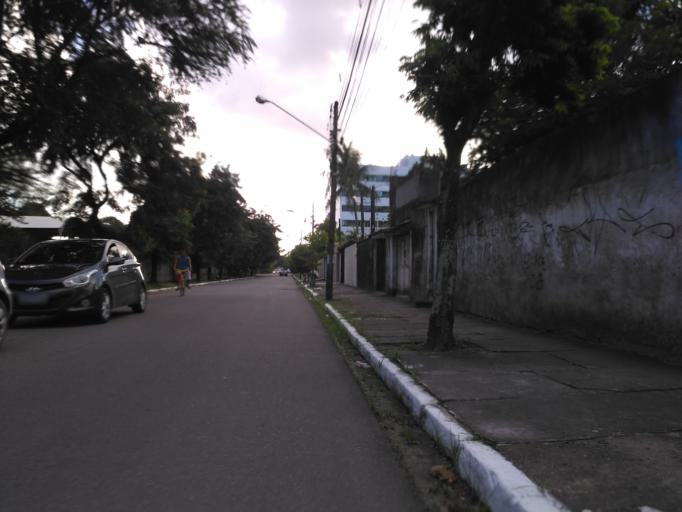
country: BR
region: Pernambuco
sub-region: Recife
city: Recife
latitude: -8.0524
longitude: -34.9415
